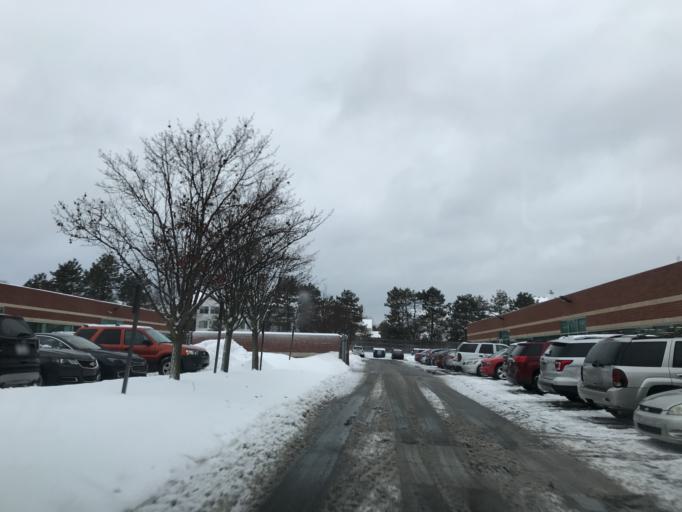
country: US
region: Michigan
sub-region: Oakland County
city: Bingham Farms
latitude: 42.4875
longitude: -83.2953
